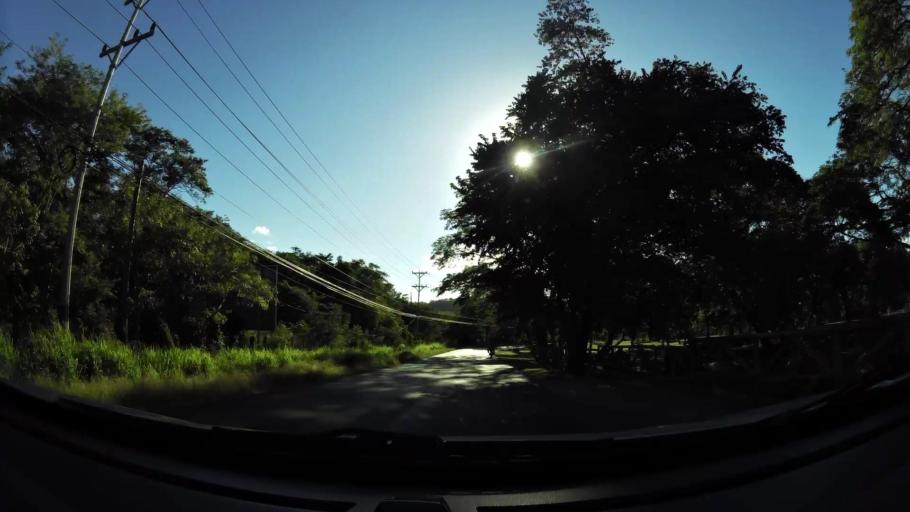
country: CR
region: Guanacaste
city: Sardinal
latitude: 10.5364
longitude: -85.6647
